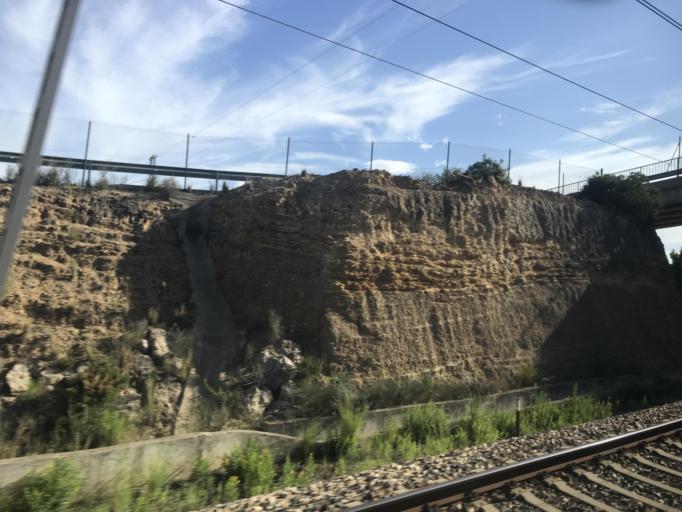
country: ES
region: Catalonia
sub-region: Provincia de Tarragona
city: L'Ampolla
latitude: 40.8301
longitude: 0.7376
